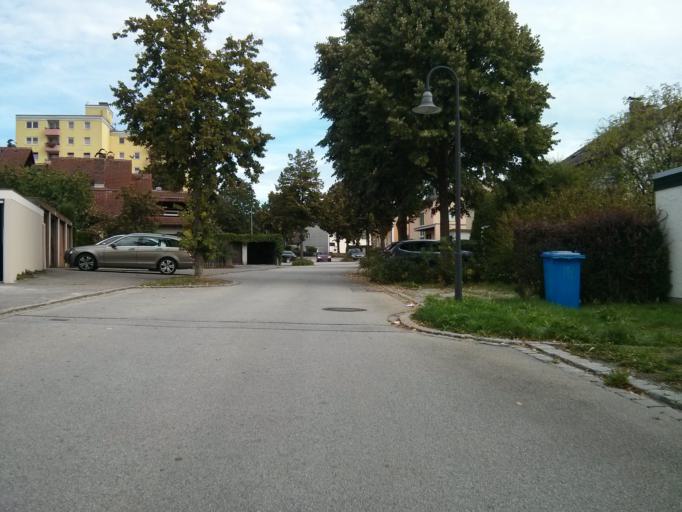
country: DE
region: Bavaria
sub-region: Lower Bavaria
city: Deggendorf
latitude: 48.8469
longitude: 12.9712
